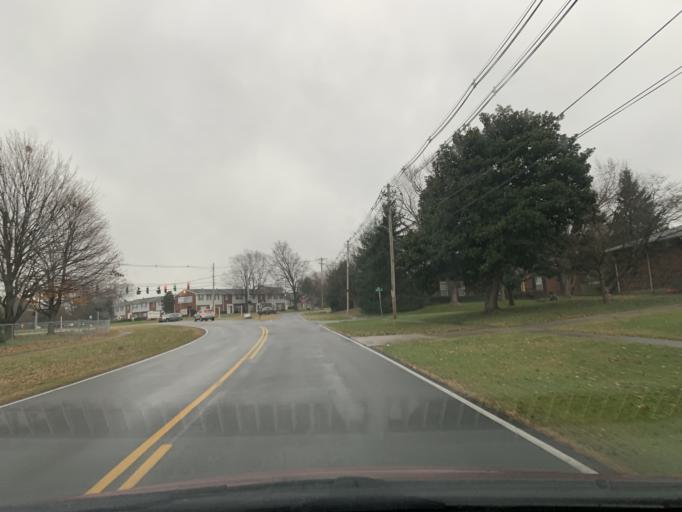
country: US
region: Kentucky
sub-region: Jefferson County
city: Saint Regis Park
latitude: 38.2002
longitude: -85.6162
